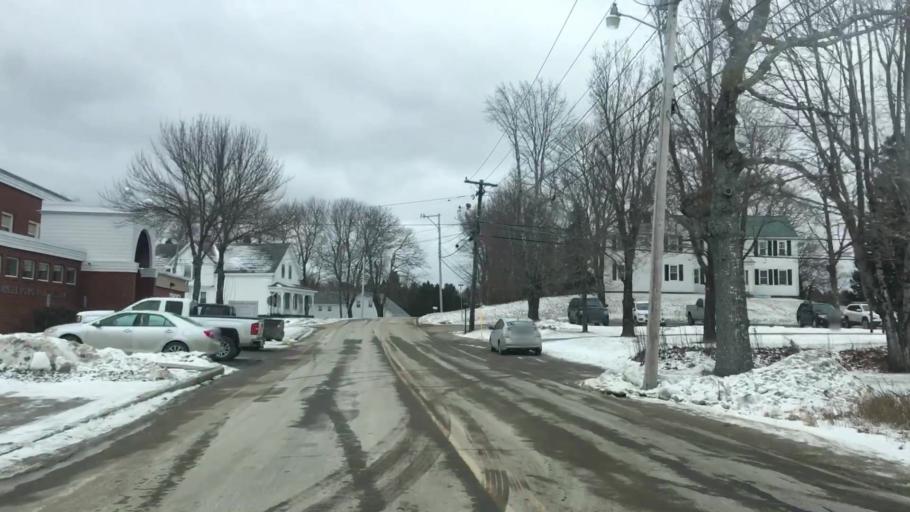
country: US
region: Maine
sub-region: Washington County
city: East Machias
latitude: 44.7346
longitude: -67.3891
